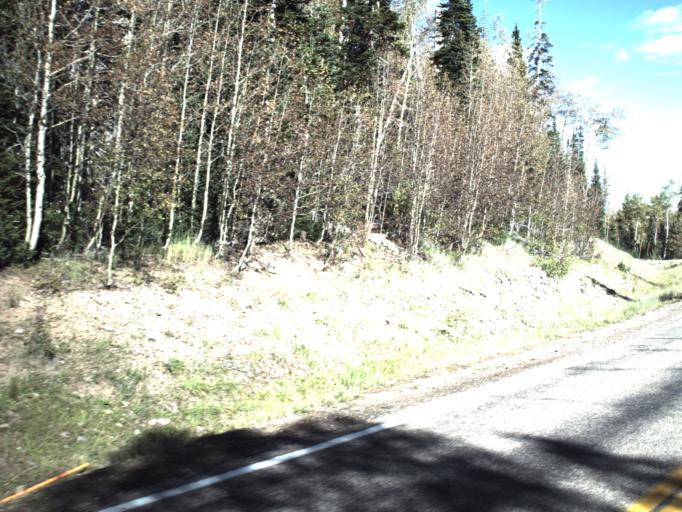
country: US
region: Utah
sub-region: Iron County
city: Parowan
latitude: 37.6555
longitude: -112.8172
